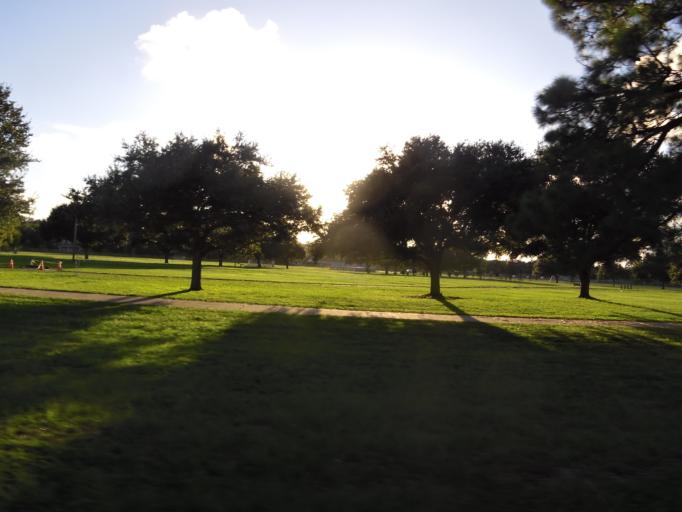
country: US
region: Georgia
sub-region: Glynn County
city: Brunswick
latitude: 31.1489
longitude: -81.4770
